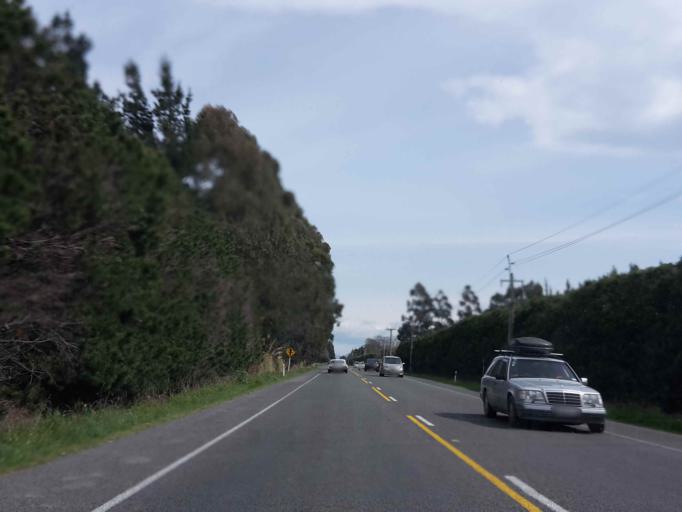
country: NZ
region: Canterbury
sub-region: Waimakariri District
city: Kaiapoi
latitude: -43.3908
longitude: 172.5777
